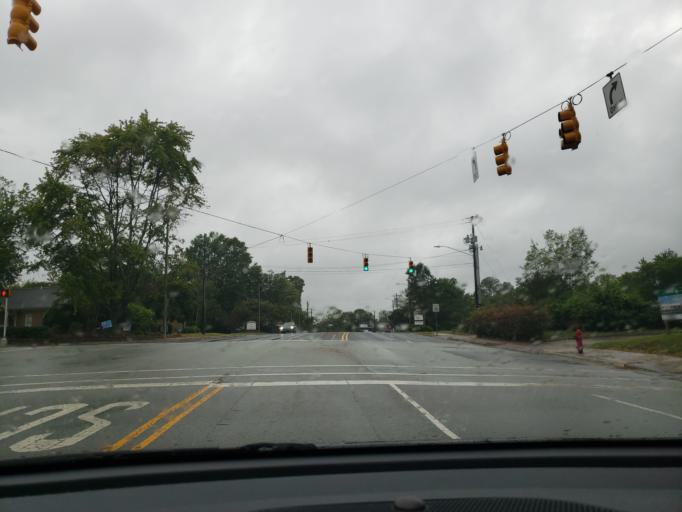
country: US
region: North Carolina
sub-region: Durham County
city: Durham
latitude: 35.9673
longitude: -78.9455
